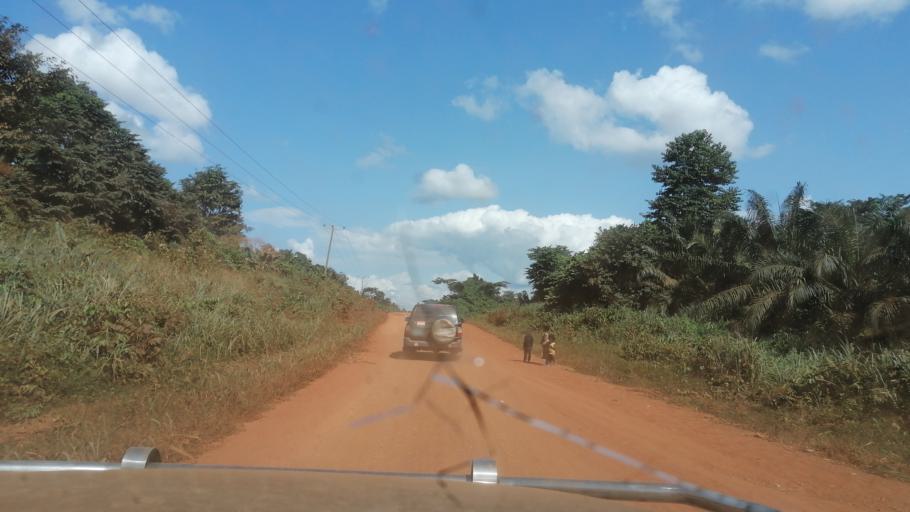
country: GH
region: Western
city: Bibiani
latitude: 6.6959
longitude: -2.5721
